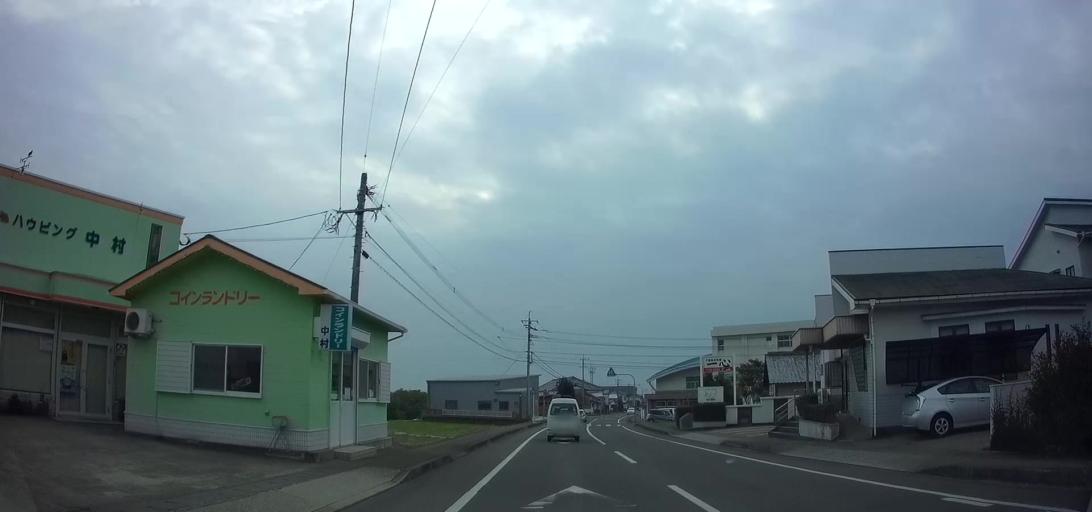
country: JP
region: Nagasaki
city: Shimabara
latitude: 32.6583
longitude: 130.2979
